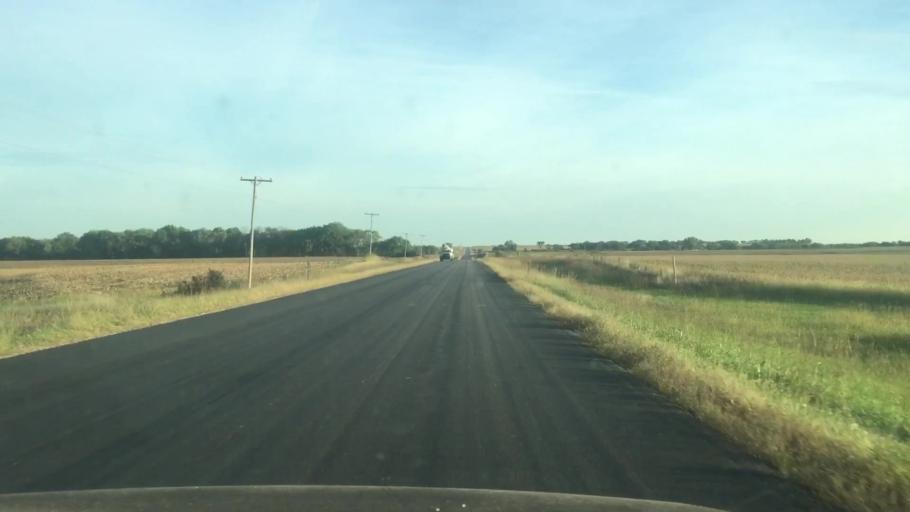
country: US
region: Kansas
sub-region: Marshall County
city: Marysville
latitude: 39.8725
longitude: -96.6009
